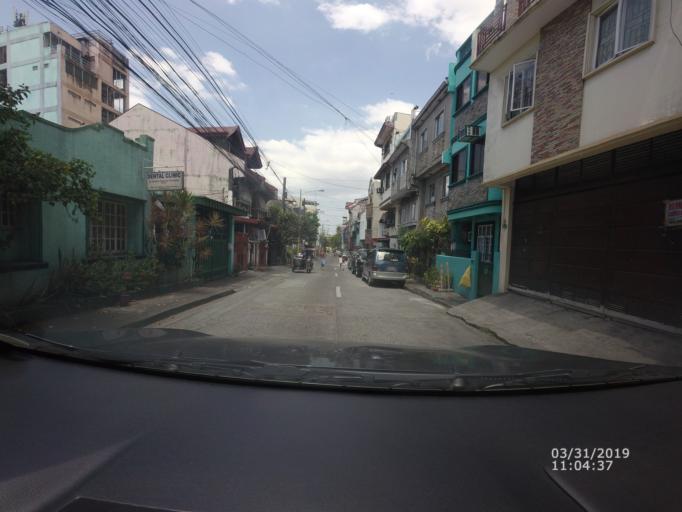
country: PH
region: Metro Manila
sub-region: Mandaluyong
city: Mandaluyong City
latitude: 14.5783
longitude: 121.0401
